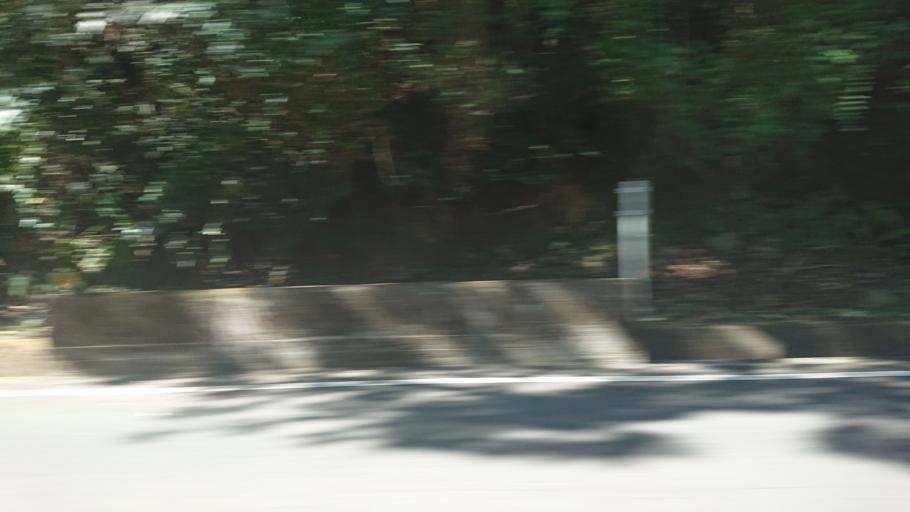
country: TW
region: Taiwan
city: Lugu
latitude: 23.4838
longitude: 120.7465
